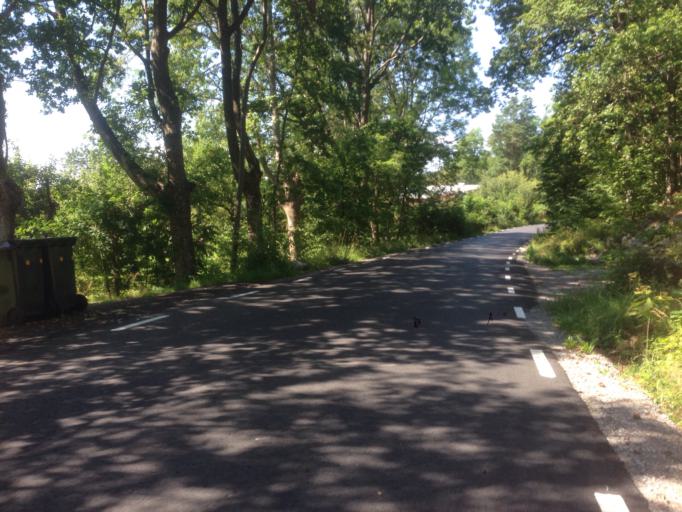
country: SE
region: Stockholm
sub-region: Vaxholms Kommun
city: Vaxholm
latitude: 59.3791
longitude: 18.3789
